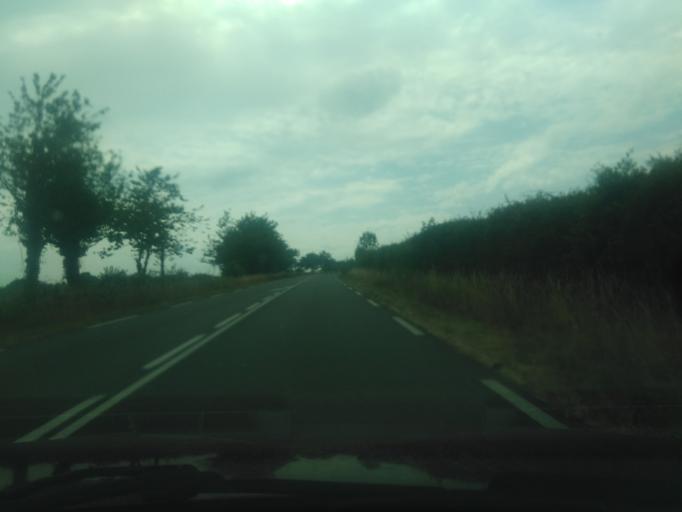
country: FR
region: Pays de la Loire
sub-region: Departement de la Vendee
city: Saint-Pierre-du-Chemin
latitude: 46.6469
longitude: -0.6534
